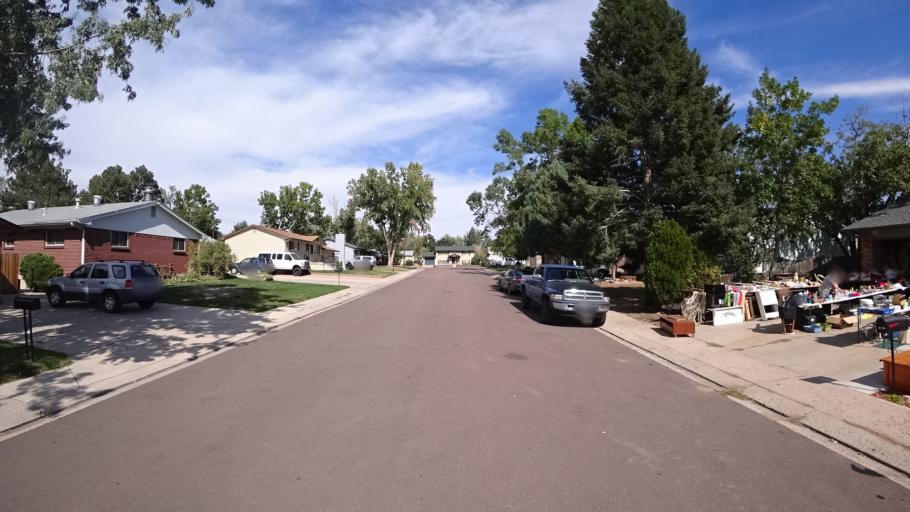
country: US
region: Colorado
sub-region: El Paso County
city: Cimarron Hills
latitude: 38.8961
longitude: -104.7625
